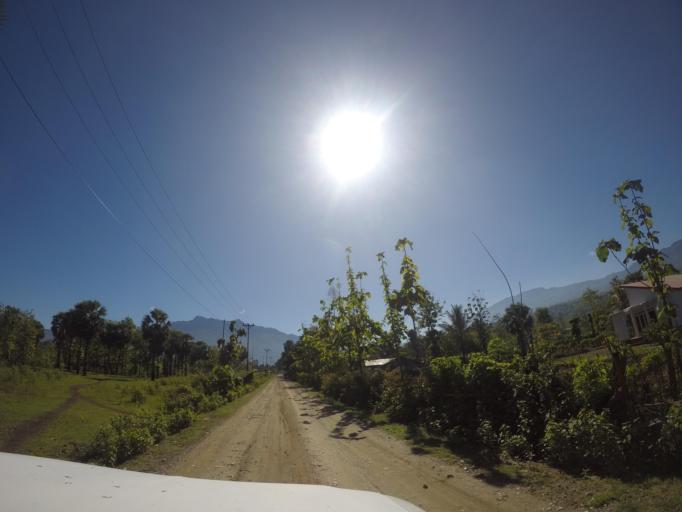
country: TL
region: Bobonaro
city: Maliana
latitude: -8.9943
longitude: 125.2042
